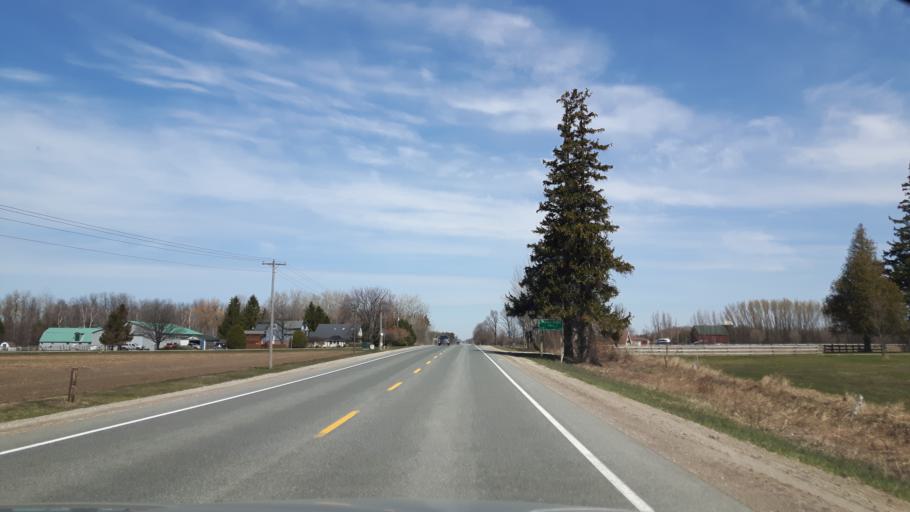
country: CA
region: Ontario
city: Goderich
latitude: 43.6970
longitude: -81.7056
